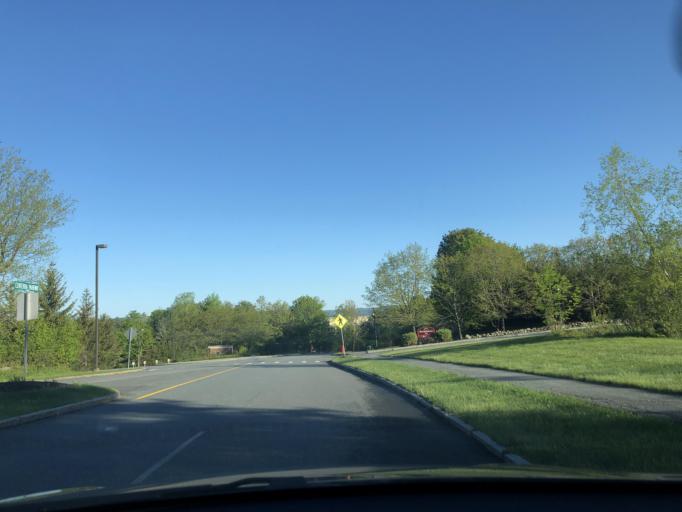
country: US
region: New Hampshire
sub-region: Grafton County
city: Lebanon
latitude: 43.6765
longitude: -72.2635
